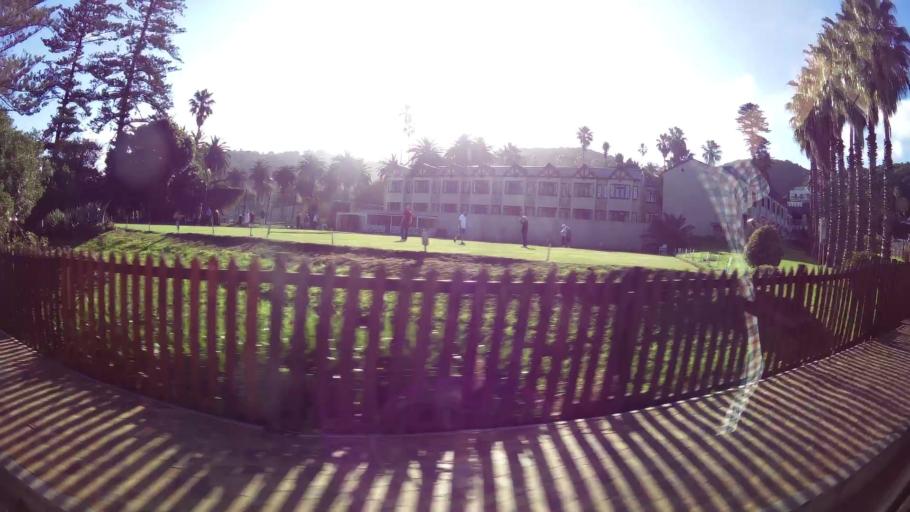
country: ZA
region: Western Cape
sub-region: Eden District Municipality
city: George
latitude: -33.9940
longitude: 22.5772
